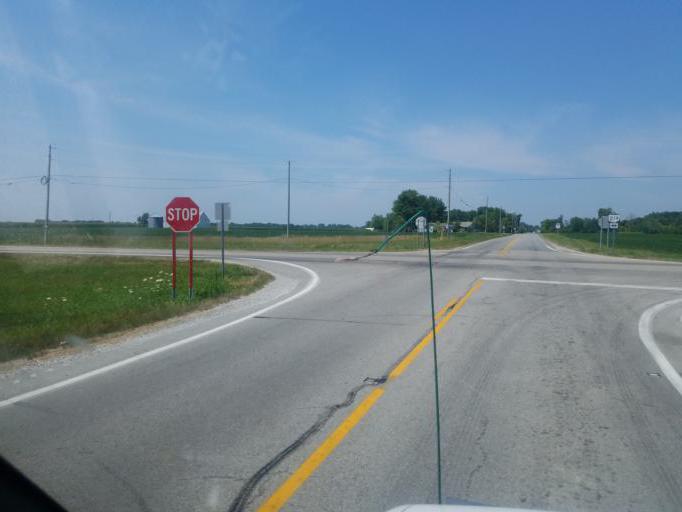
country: US
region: Ohio
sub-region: Auglaize County
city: Saint Marys
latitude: 40.4947
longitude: -84.4345
